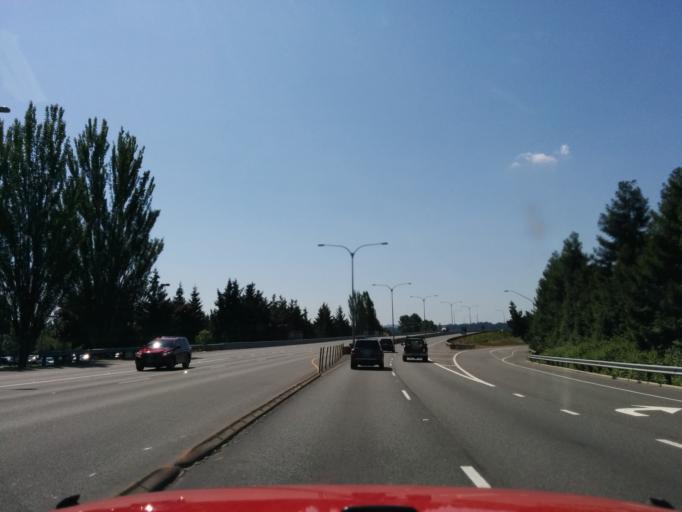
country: US
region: Washington
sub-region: King County
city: Redmond
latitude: 47.6744
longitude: -122.1059
